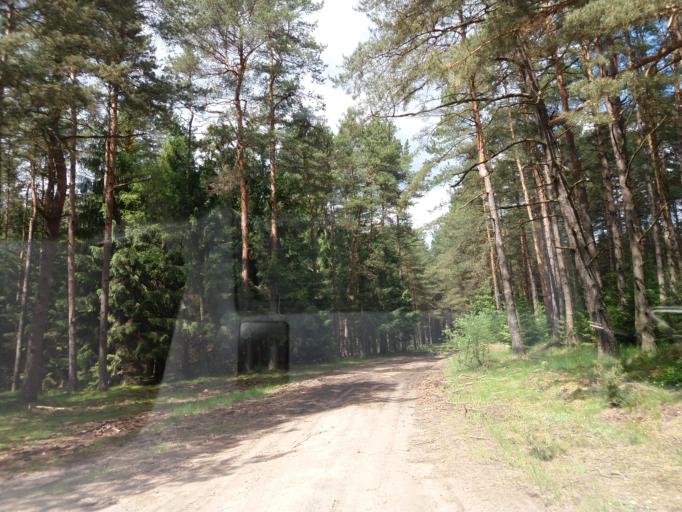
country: PL
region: West Pomeranian Voivodeship
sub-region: Powiat choszczenski
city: Drawno
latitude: 53.2815
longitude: 15.7274
